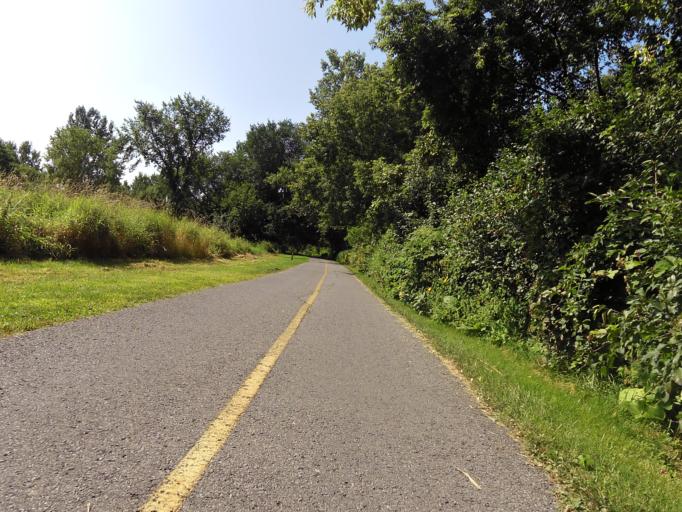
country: CA
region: Ontario
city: Ottawa
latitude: 45.4123
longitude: -75.6706
